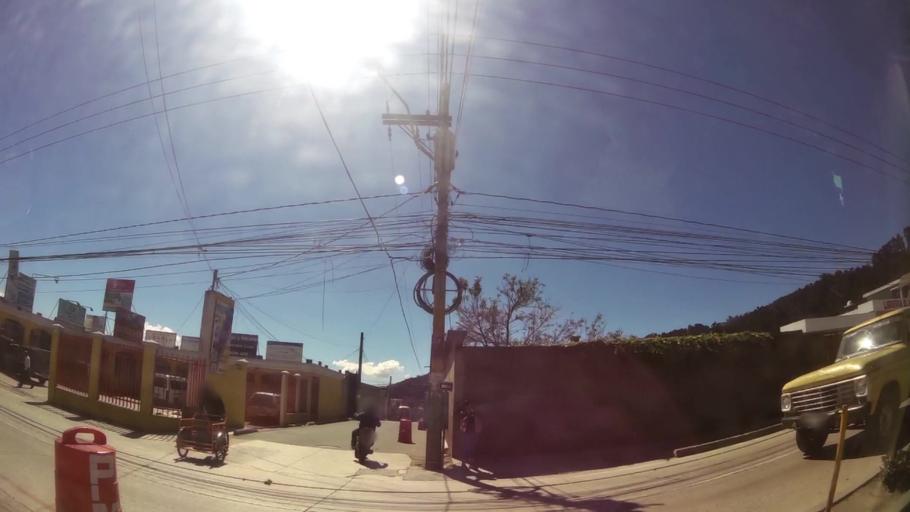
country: GT
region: Guatemala
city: San Jose Pinula
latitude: 14.5464
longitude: -90.4159
